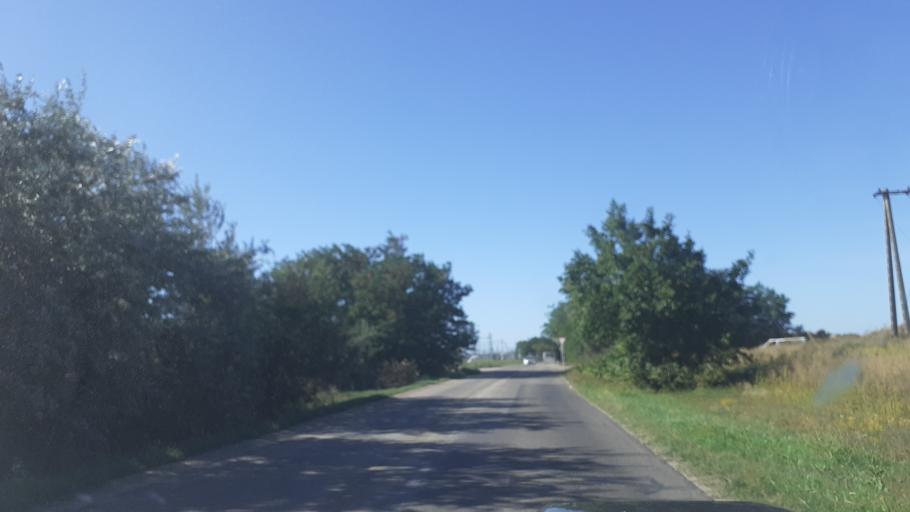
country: HU
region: Fejer
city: Pusztaszabolcs
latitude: 47.1480
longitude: 18.7694
